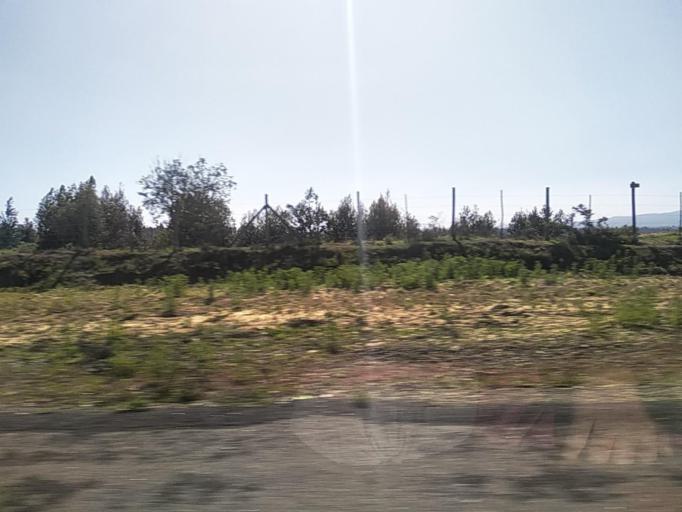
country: CL
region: Valparaiso
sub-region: San Antonio Province
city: El Tabo
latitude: -33.4075
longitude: -71.5489
